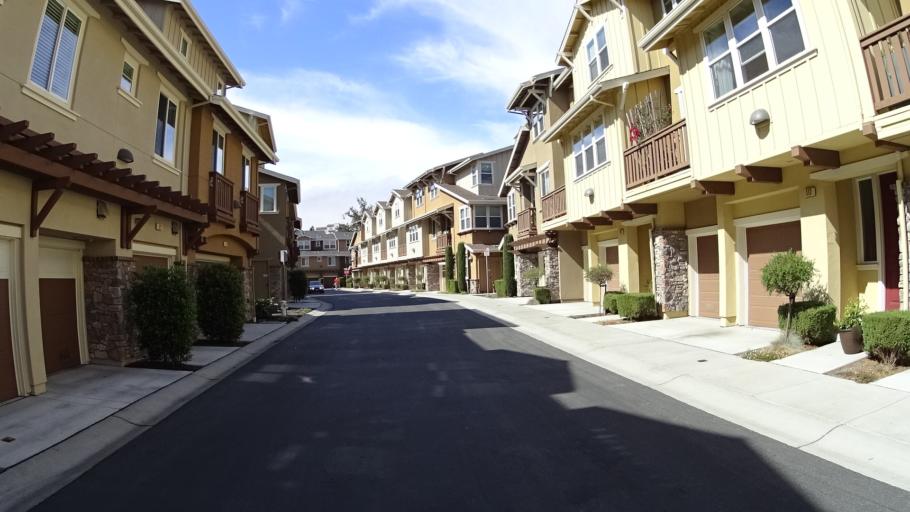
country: US
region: California
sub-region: San Mateo County
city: Brisbane
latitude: 37.7130
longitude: -122.3942
